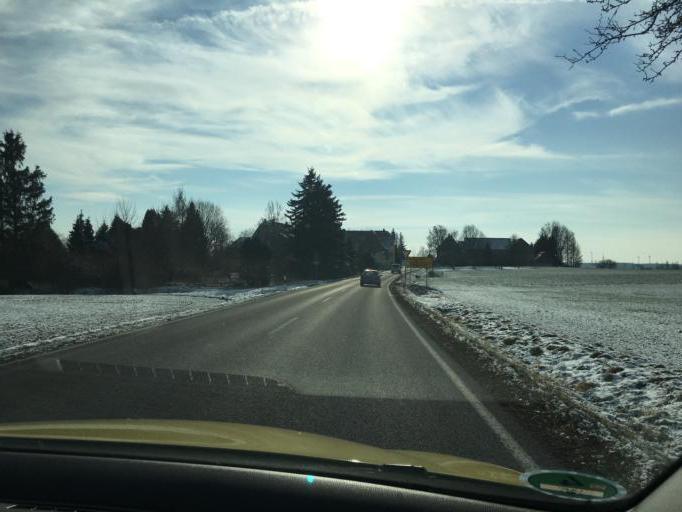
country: DE
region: Saxony
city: Narsdorf
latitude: 51.0203
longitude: 12.7310
